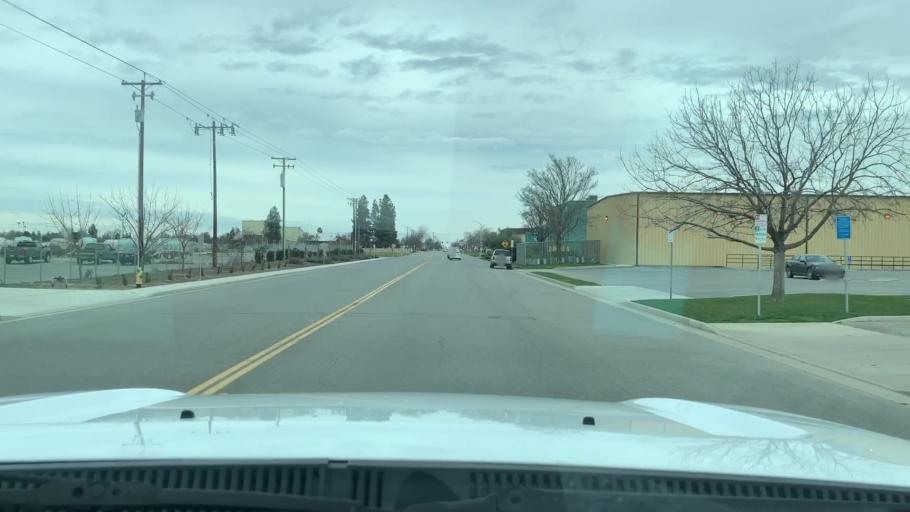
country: US
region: California
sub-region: Kern County
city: Shafter
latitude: 35.4946
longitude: -119.2606
